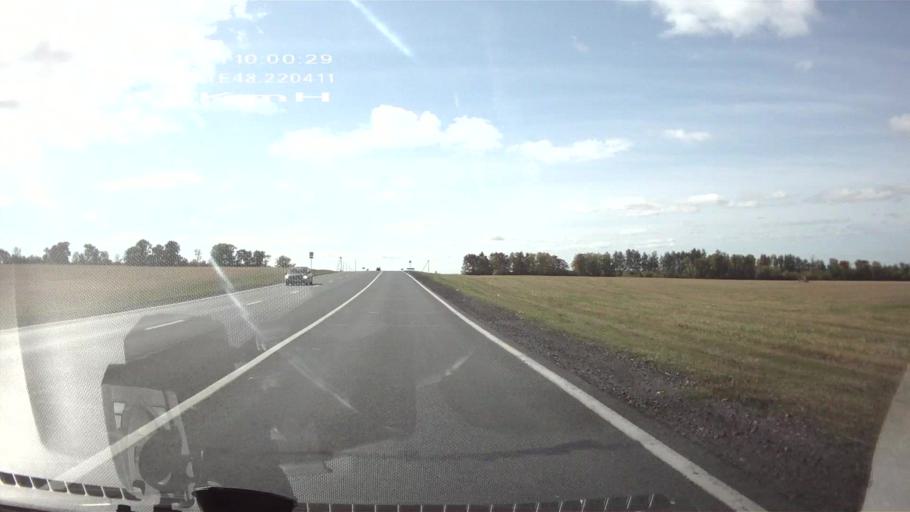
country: RU
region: Ulyanovsk
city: Krasnyy Gulyay
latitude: 54.0623
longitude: 48.2205
